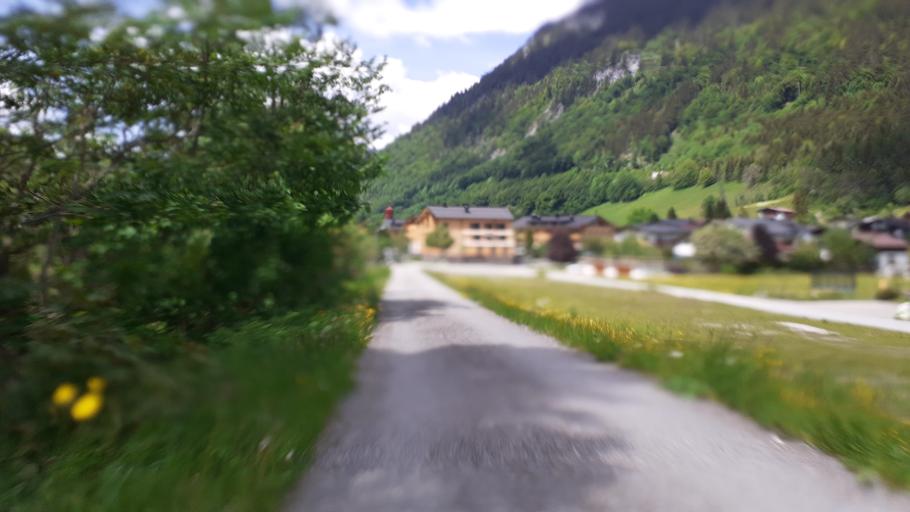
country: AT
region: Vorarlberg
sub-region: Politischer Bezirk Bludenz
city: Klosterle
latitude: 47.1304
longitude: 10.0958
